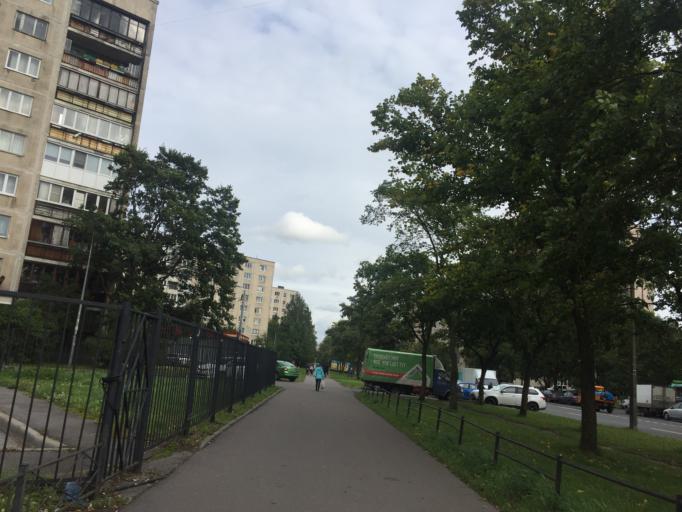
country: RU
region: St.-Petersburg
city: Shushary
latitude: 59.8289
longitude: 30.3873
